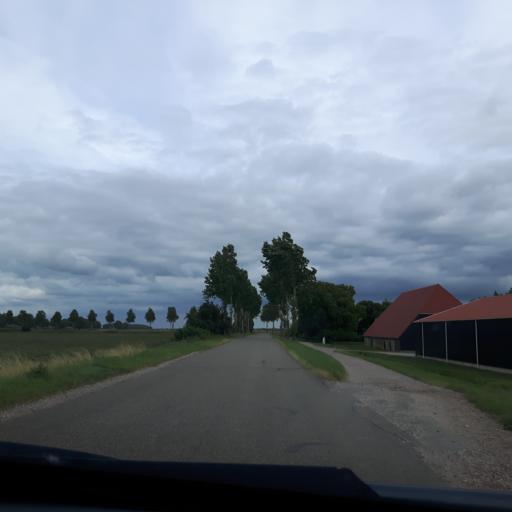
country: NL
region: Zeeland
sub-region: Gemeente Noord-Beveland
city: Kamperland
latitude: 51.5570
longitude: 3.7457
